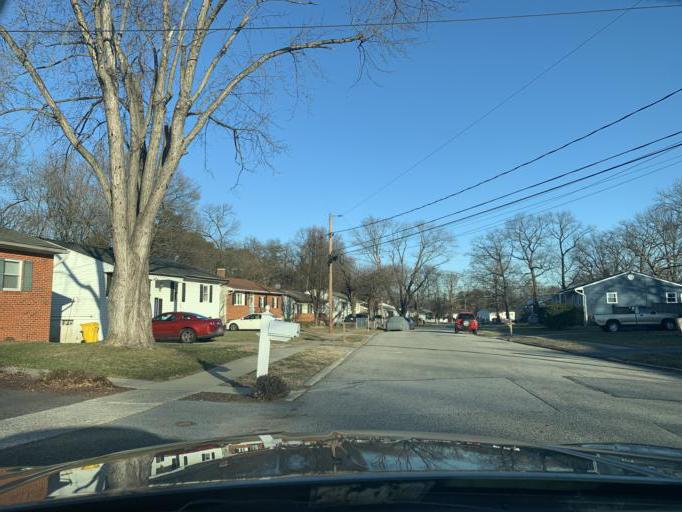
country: US
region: Maryland
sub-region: Anne Arundel County
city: Glen Burnie
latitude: 39.1475
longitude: -76.6177
